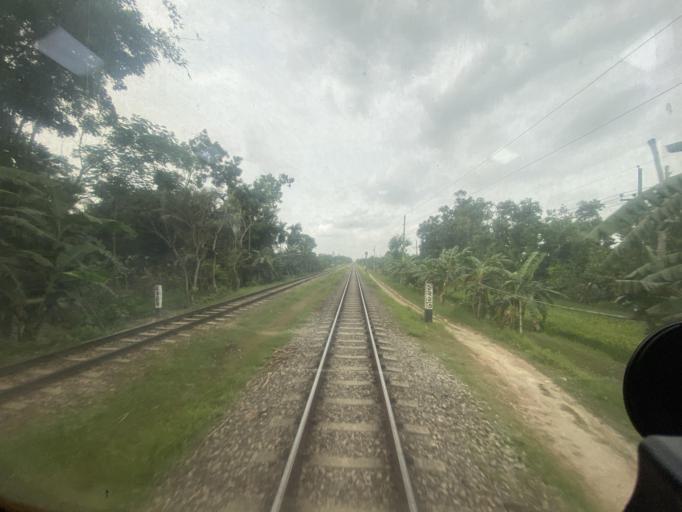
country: BD
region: Chittagong
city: Laksham
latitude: 23.1961
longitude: 91.1650
